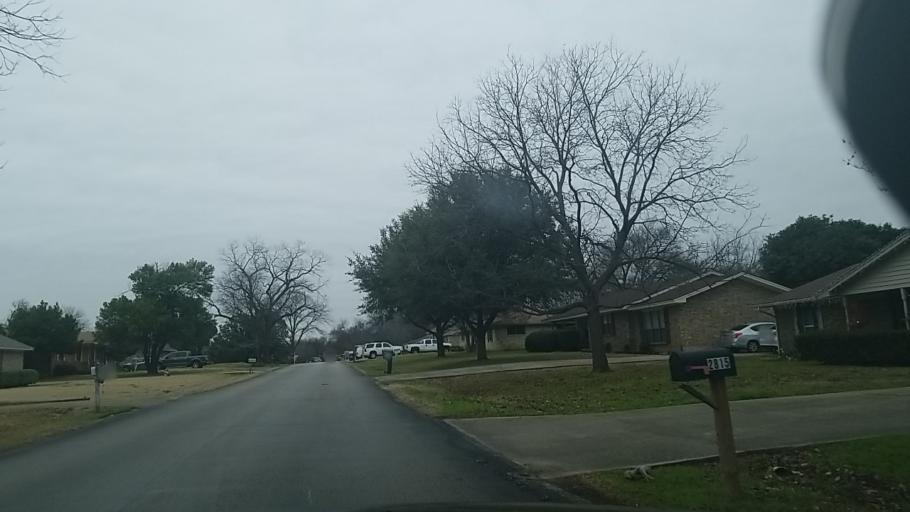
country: US
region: Texas
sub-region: Denton County
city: Corinth
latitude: 33.1489
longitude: -97.0624
